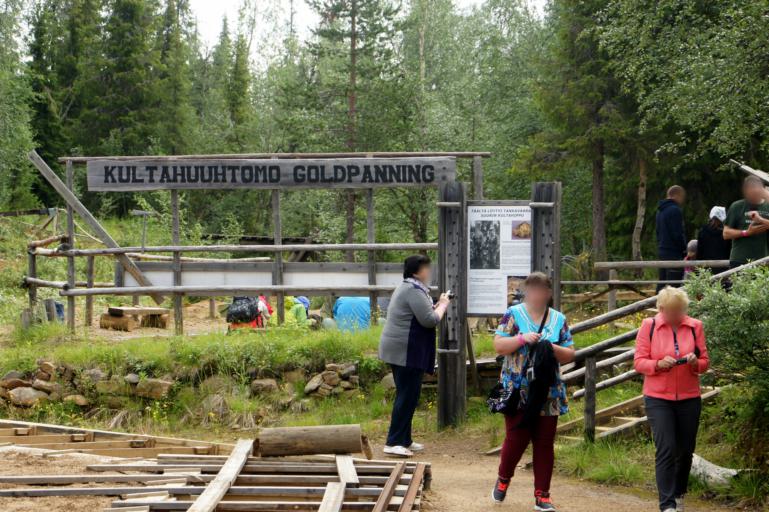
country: FI
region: Lapland
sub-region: Pohjois-Lappi
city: Ivalo
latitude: 68.1791
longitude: 27.1065
